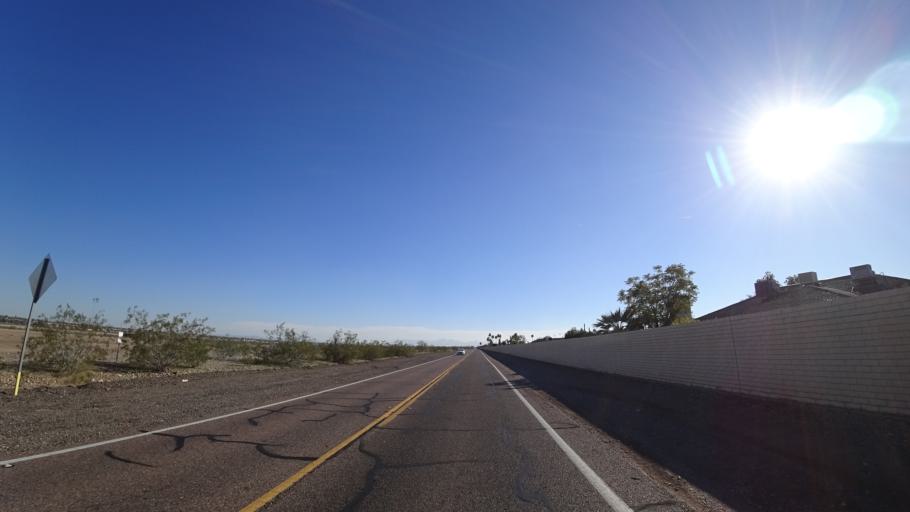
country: US
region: Arizona
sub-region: Maricopa County
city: Sun City West
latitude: 33.6610
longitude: -112.3251
